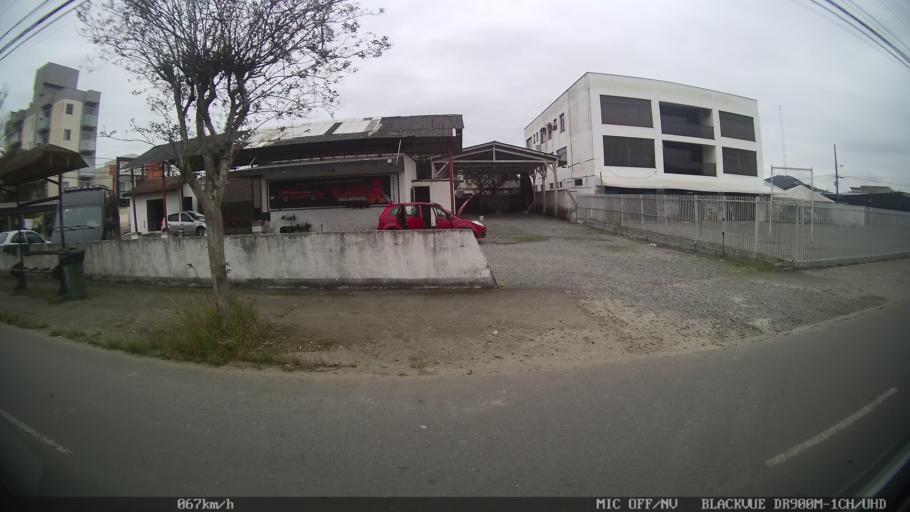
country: BR
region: Santa Catarina
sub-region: Joinville
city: Joinville
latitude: -26.3232
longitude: -48.8354
